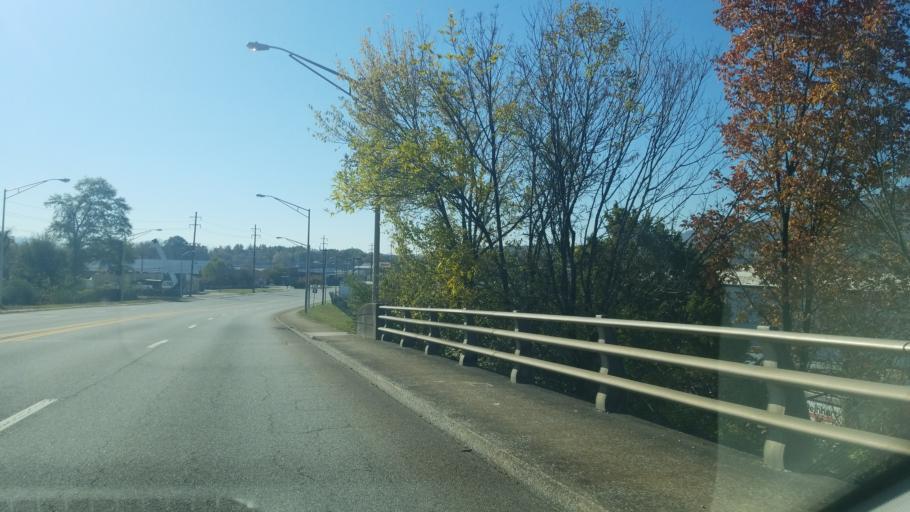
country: US
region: Tennessee
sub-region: Hamilton County
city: Chattanooga
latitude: 35.0216
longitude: -85.3114
